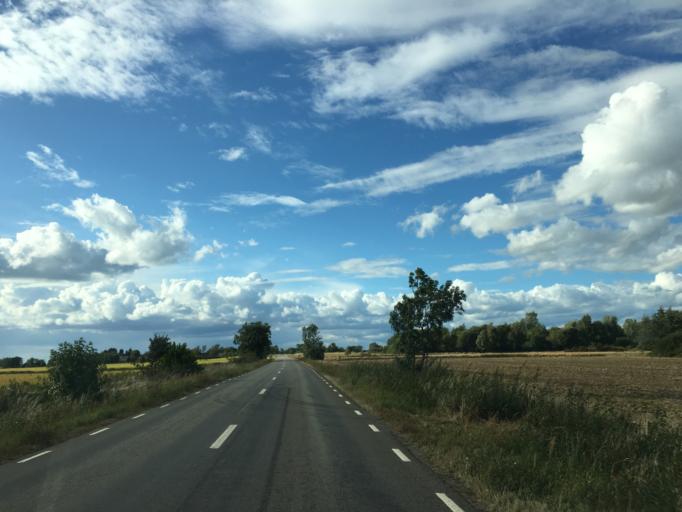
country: SE
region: Kalmar
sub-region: Morbylanga Kommun
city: Moerbylanga
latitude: 56.4375
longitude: 16.4326
